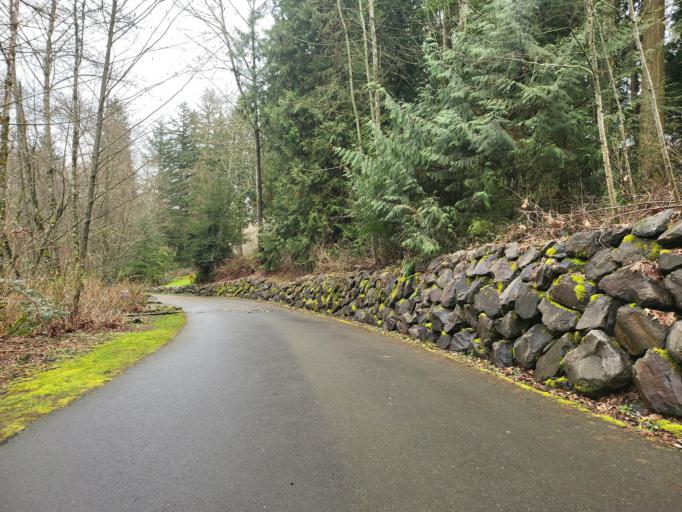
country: US
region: Washington
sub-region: King County
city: East Hill-Meridian
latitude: 47.4215
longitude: -122.1673
